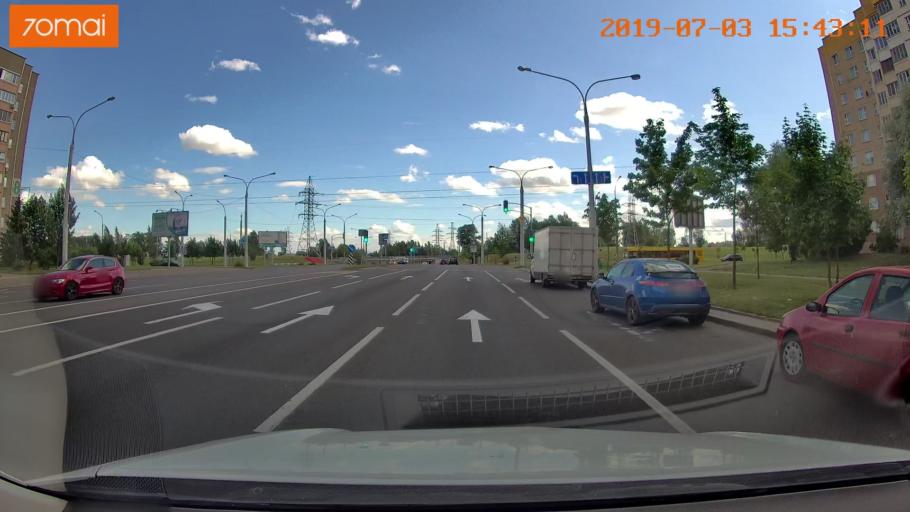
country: BY
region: Minsk
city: Syenitsa
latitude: 53.8362
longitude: 27.5744
